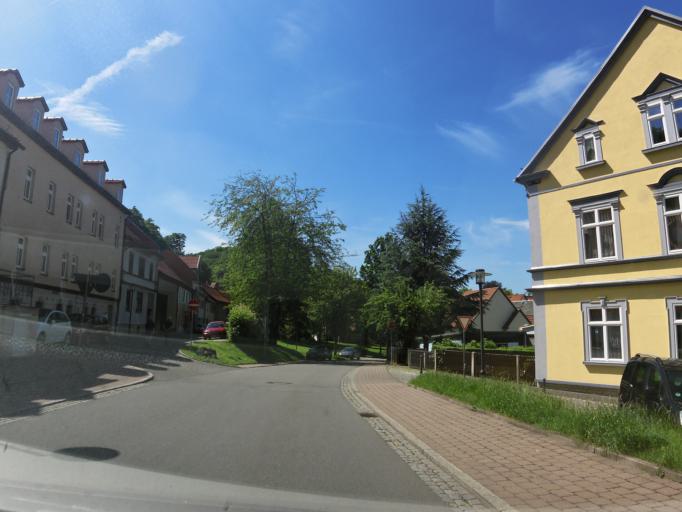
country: DE
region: Thuringia
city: Waltershausen
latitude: 50.8964
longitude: 10.5549
